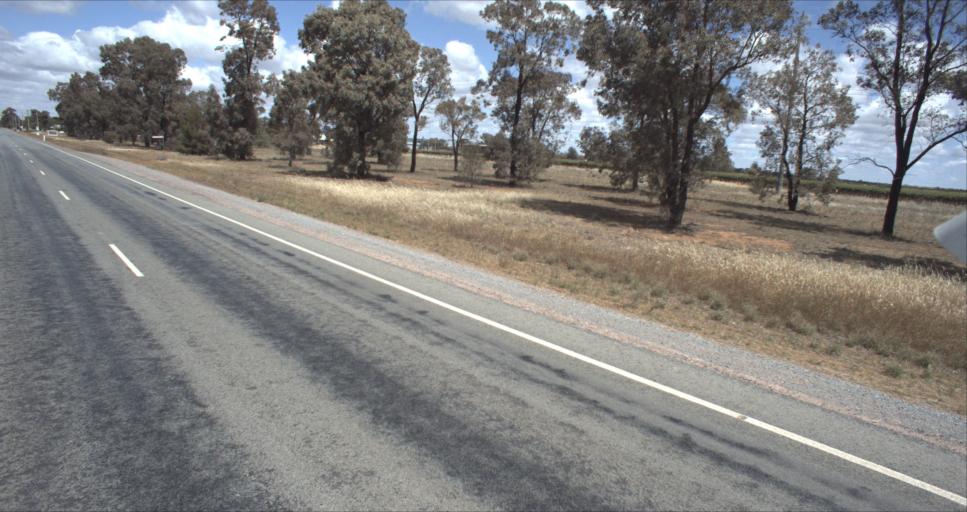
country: AU
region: New South Wales
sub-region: Murrumbidgee Shire
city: Darlington Point
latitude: -34.5073
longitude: 146.1870
